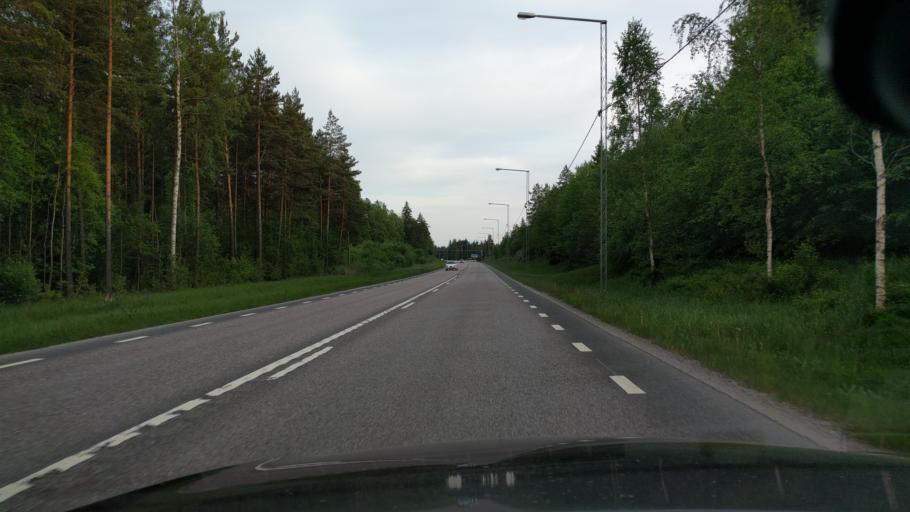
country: SE
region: Stockholm
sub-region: Vallentuna Kommun
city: Vallentuna
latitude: 59.5202
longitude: 18.0939
